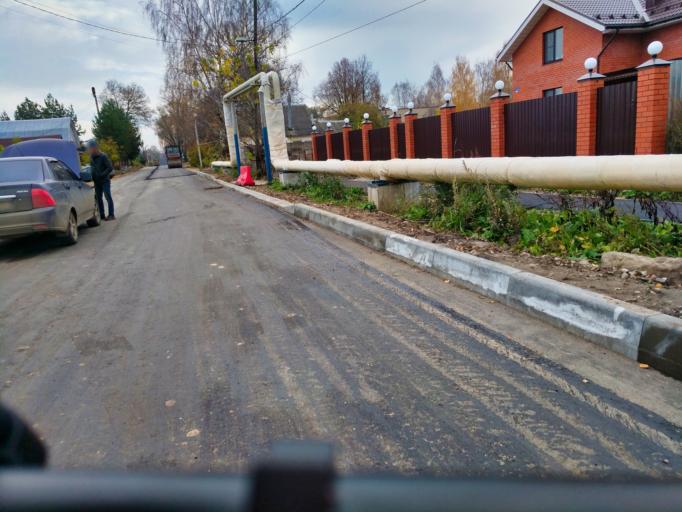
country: RU
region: Tverskaya
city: Rzhev
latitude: 56.2490
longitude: 34.3356
